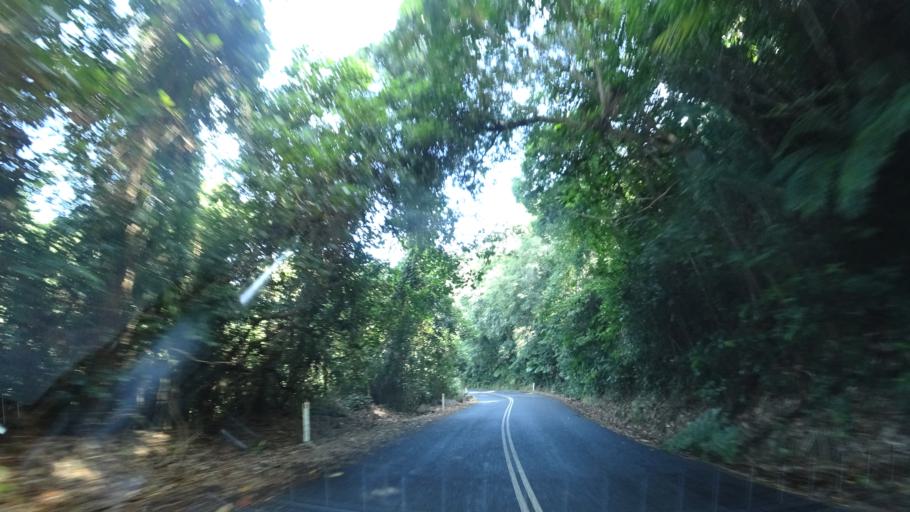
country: AU
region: Queensland
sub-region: Cairns
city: Port Douglas
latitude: -16.1279
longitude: 145.4551
